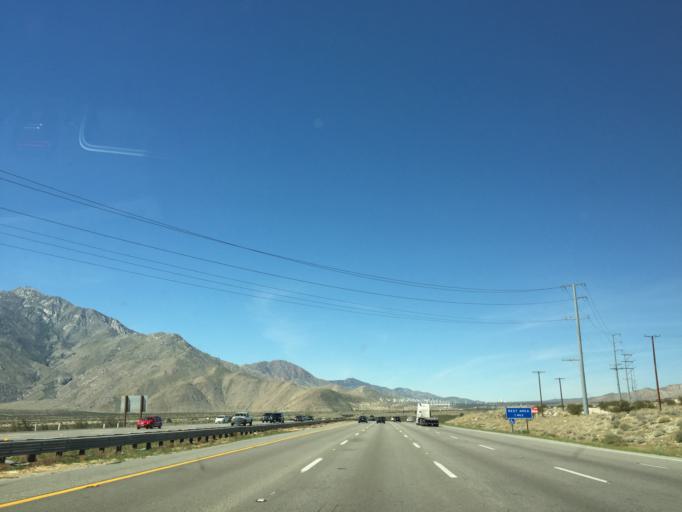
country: US
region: California
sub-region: Riverside County
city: Garnet
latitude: 33.9229
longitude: -116.6494
